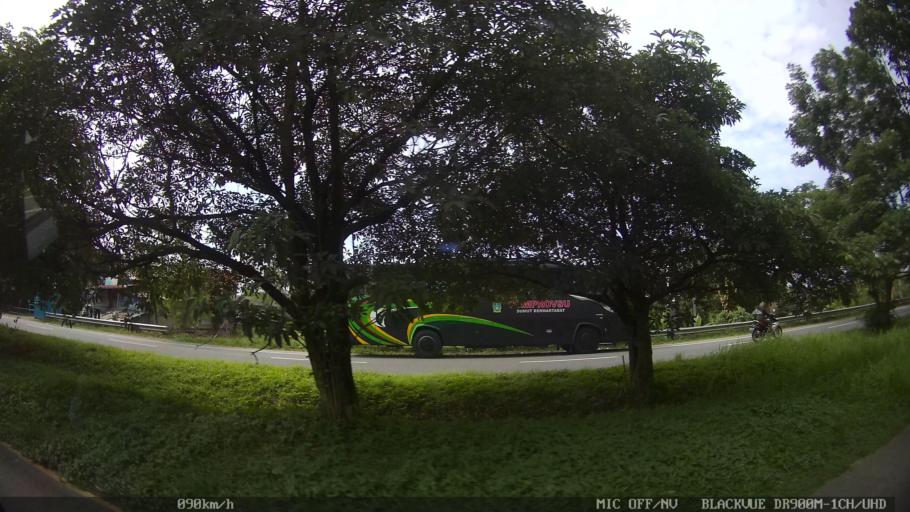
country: ID
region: North Sumatra
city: Percut
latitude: 3.5991
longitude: 98.8283
